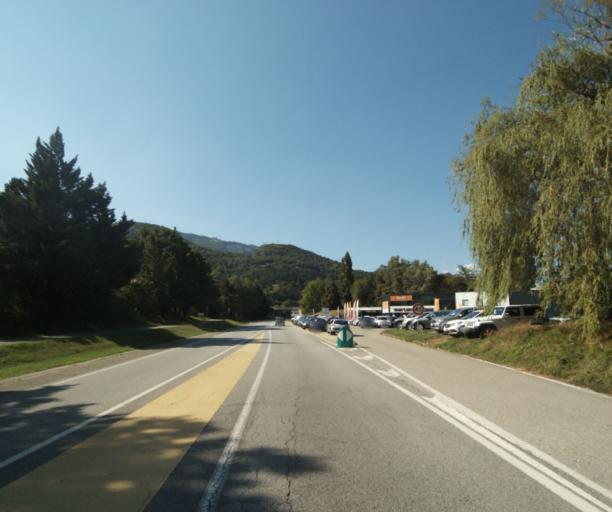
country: FR
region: Rhone-Alpes
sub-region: Departement de l'Isere
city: Seyssinet-Pariset
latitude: 45.1689
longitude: 5.6898
